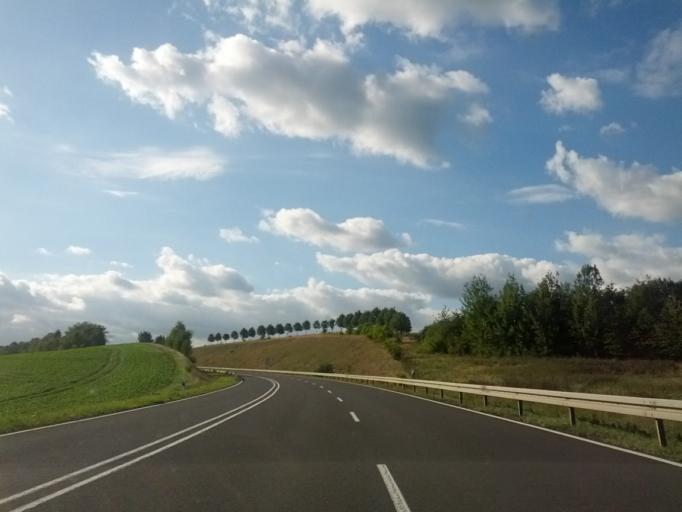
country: DE
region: Thuringia
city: Barchfeld
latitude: 50.8135
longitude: 10.3014
